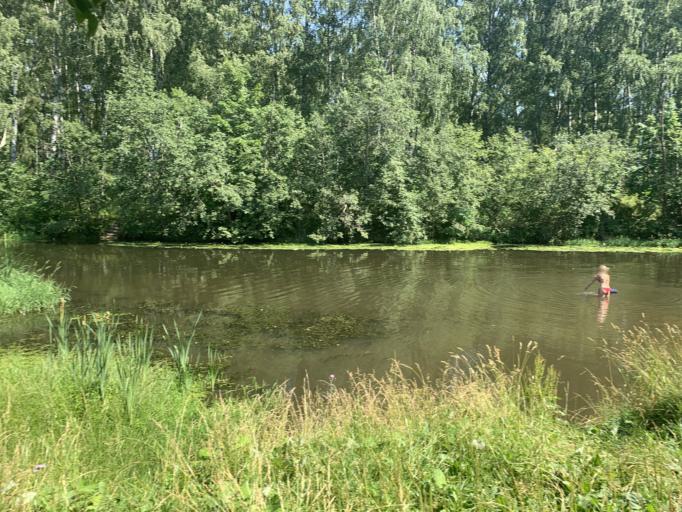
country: RU
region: Moskovskaya
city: Mamontovka
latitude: 55.9692
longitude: 37.8200
